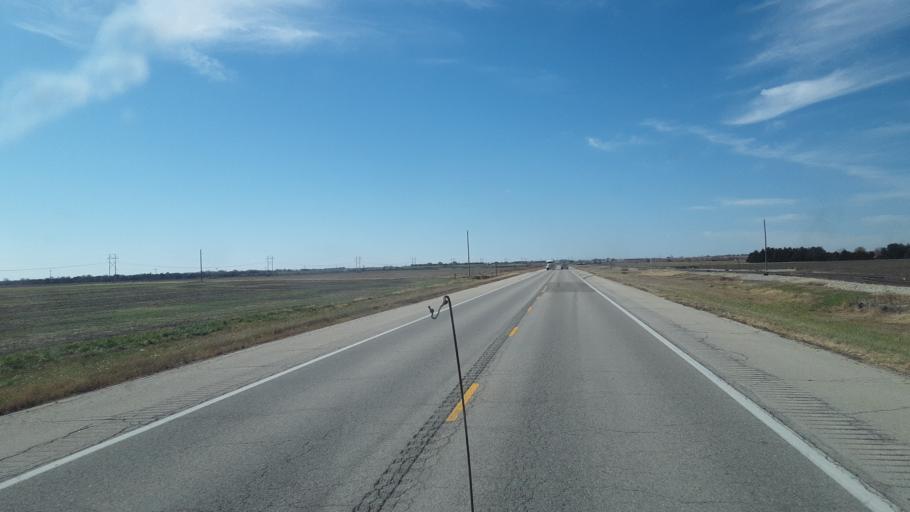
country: US
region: Kansas
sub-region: McPherson County
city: McPherson
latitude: 38.3663
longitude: -97.7382
